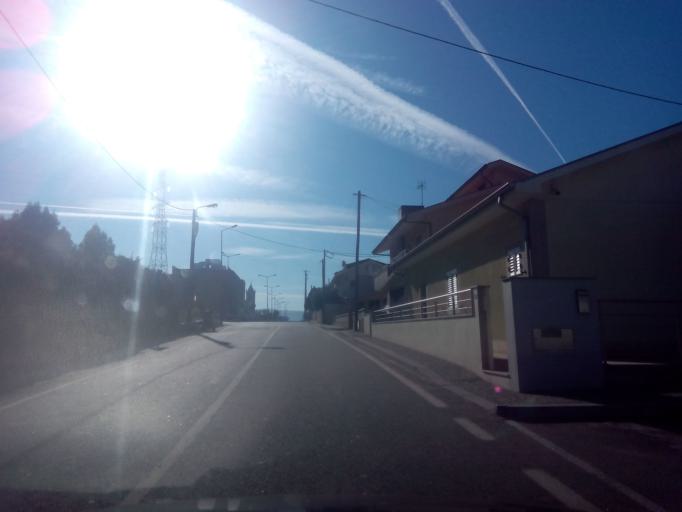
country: PT
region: Porto
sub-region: Paredes
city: Gandra
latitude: 41.2030
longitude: -8.4428
